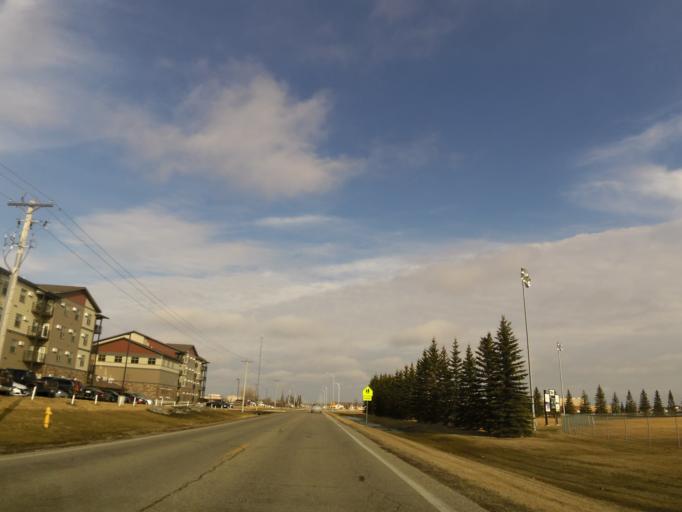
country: US
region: North Dakota
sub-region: Grand Forks County
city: Grand Forks
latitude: 47.8749
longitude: -97.0610
